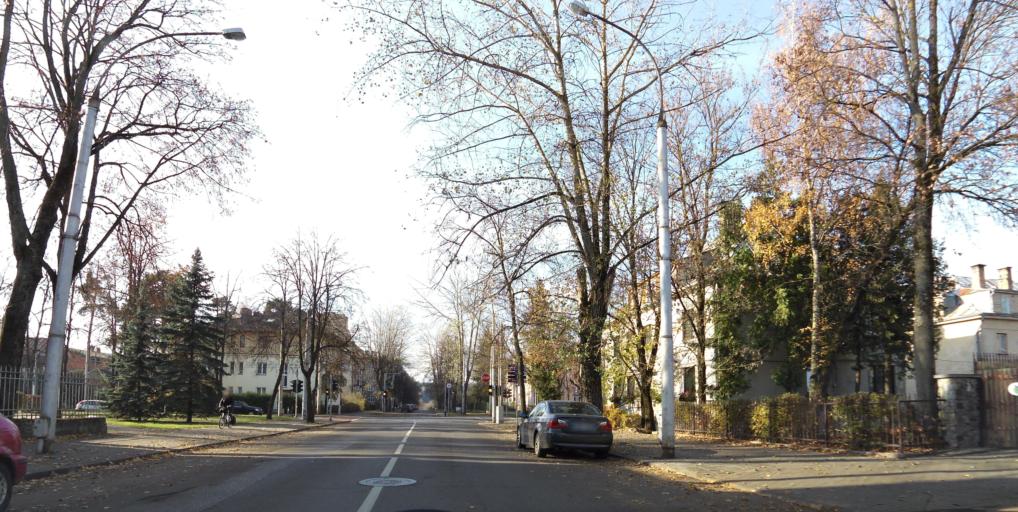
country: LT
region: Vilnius County
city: Naujamiestis
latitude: 54.6901
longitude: 25.2527
